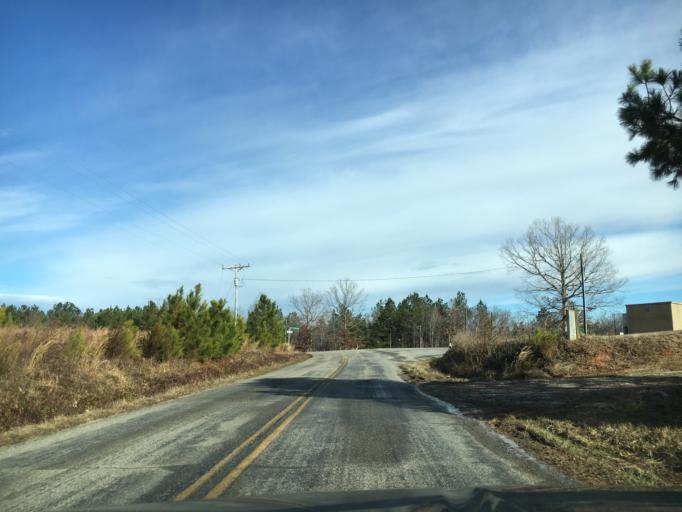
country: US
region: Virginia
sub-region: Nottoway County
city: Crewe
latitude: 37.3313
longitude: -78.1625
